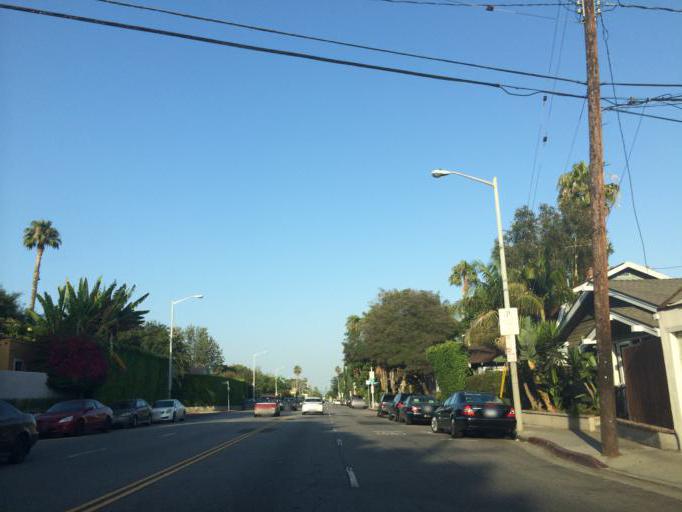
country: US
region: California
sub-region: Los Angeles County
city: West Hollywood
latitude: 34.0944
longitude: -118.3600
